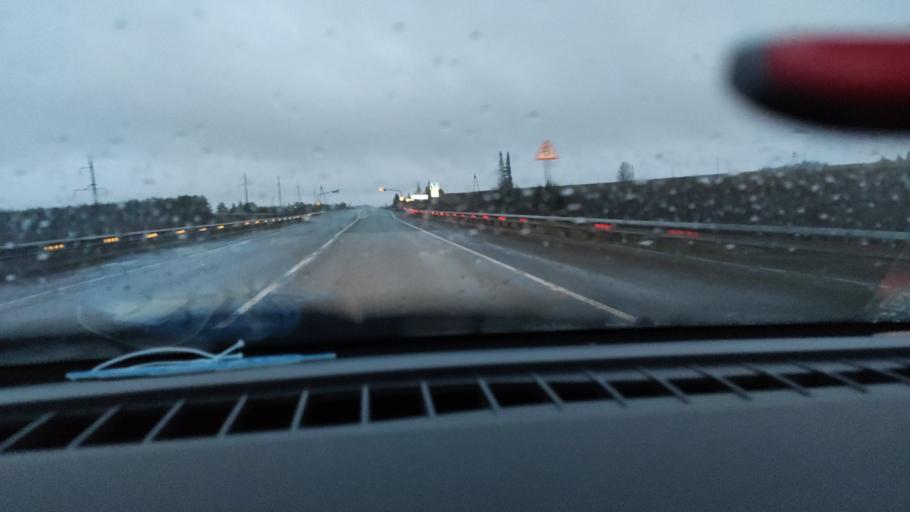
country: RU
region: Udmurtiya
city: Alnashi
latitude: 56.2338
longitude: 52.4028
